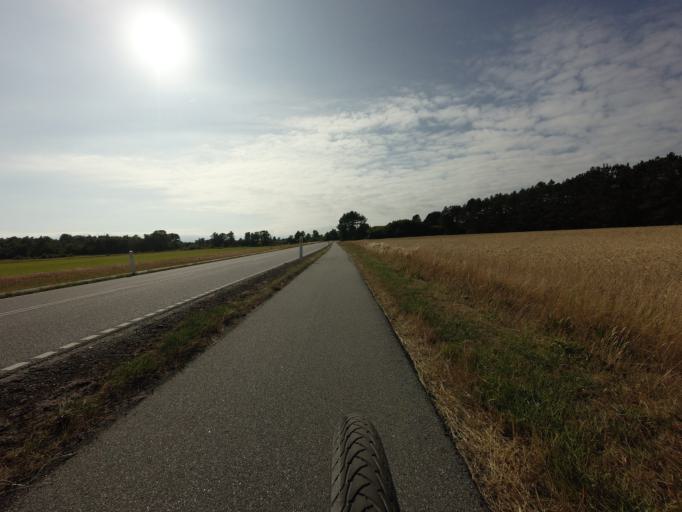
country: DK
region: North Denmark
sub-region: Laeso Kommune
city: Byrum
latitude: 57.2761
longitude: 10.9409
